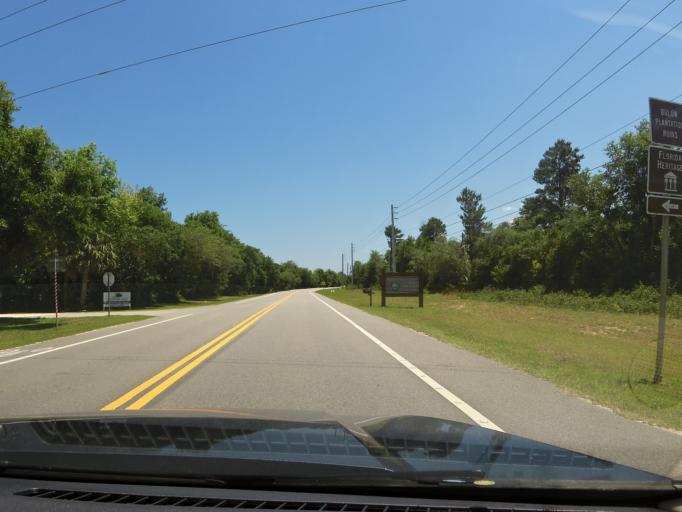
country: US
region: Florida
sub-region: Flagler County
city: Flagler Beach
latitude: 29.4307
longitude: -81.1538
